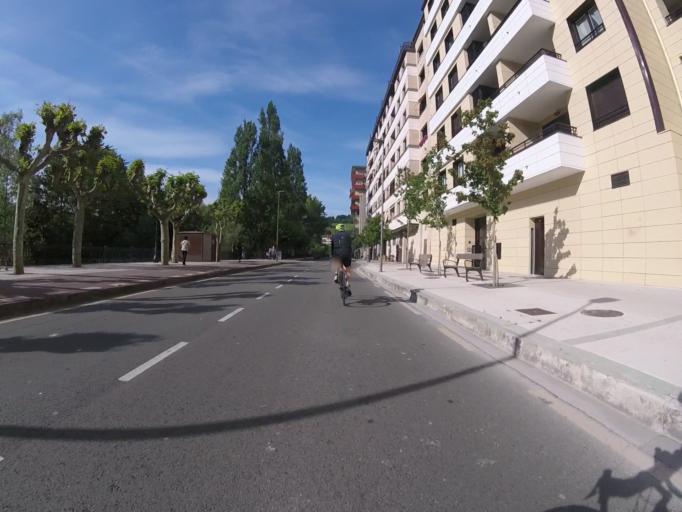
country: ES
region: Basque Country
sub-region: Provincia de Guipuzcoa
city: Beasain
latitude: 43.0495
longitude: -2.1907
